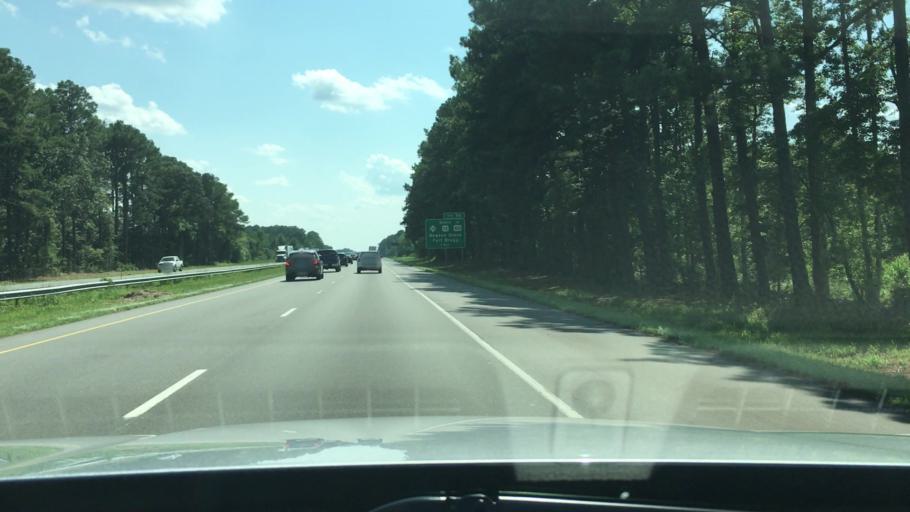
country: US
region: North Carolina
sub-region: Cumberland County
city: Eastover
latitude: 35.1393
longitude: -78.7374
